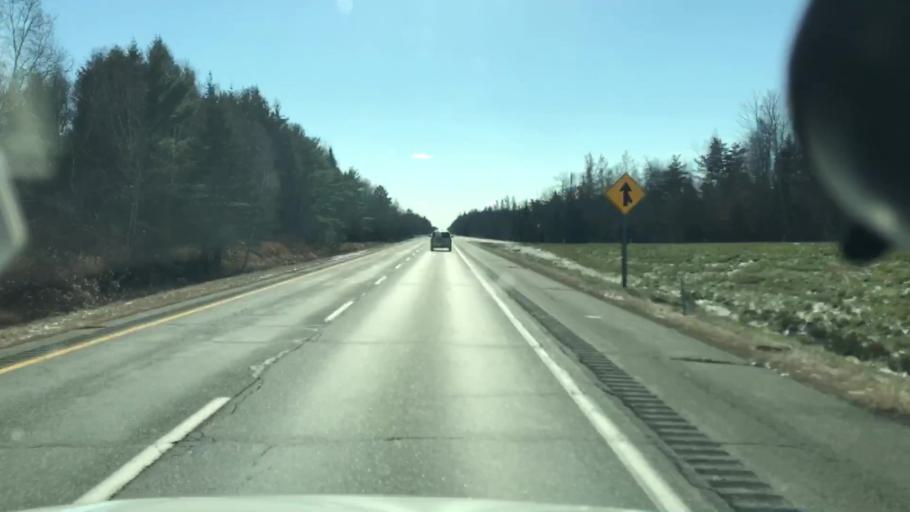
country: US
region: Maine
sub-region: Penobscot County
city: Milford
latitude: 44.9945
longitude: -68.7027
